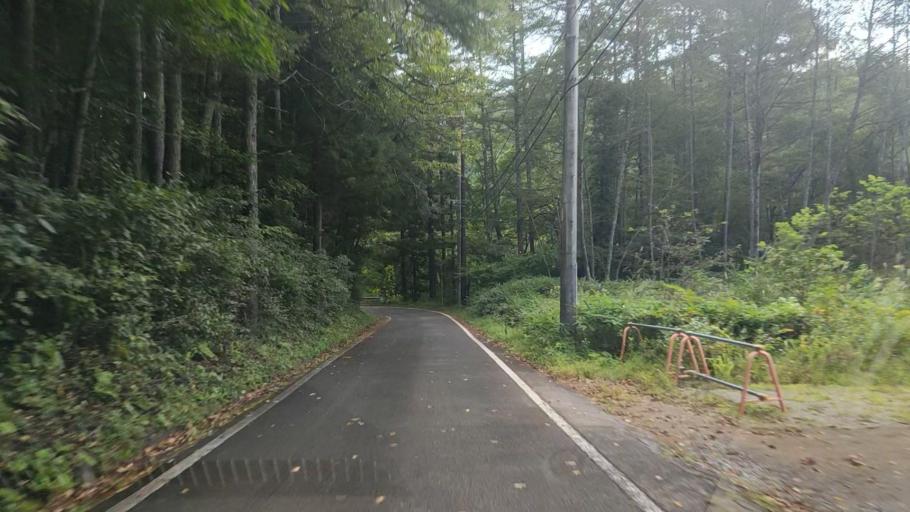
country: JP
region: Gunma
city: Nakanojomachi
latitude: 36.6555
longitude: 138.6341
